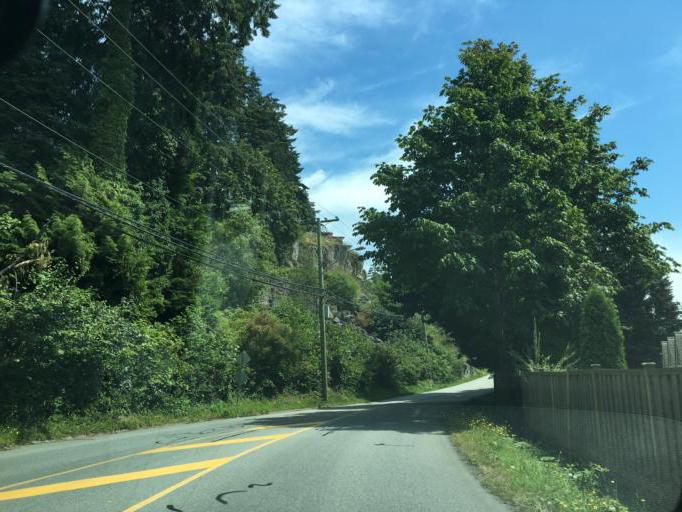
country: CA
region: British Columbia
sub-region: Greater Vancouver Regional District
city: Bowen Island
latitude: 49.3409
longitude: -123.2583
